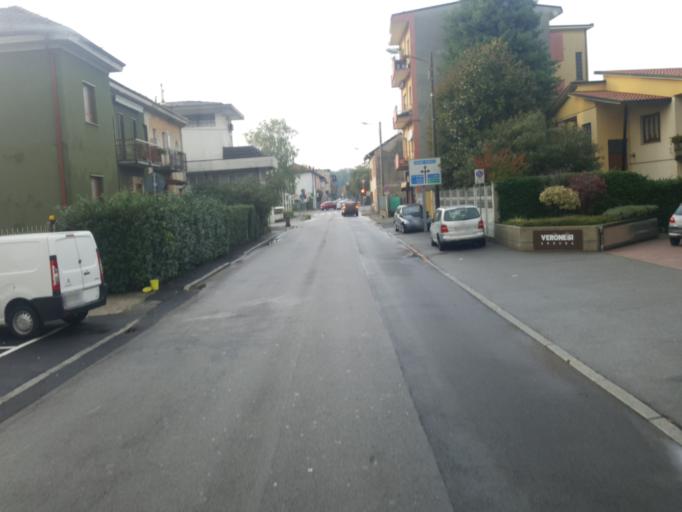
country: IT
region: Lombardy
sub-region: Provincia di Monza e Brianza
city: Bovisio-Masciago
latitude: 45.6141
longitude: 9.1391
